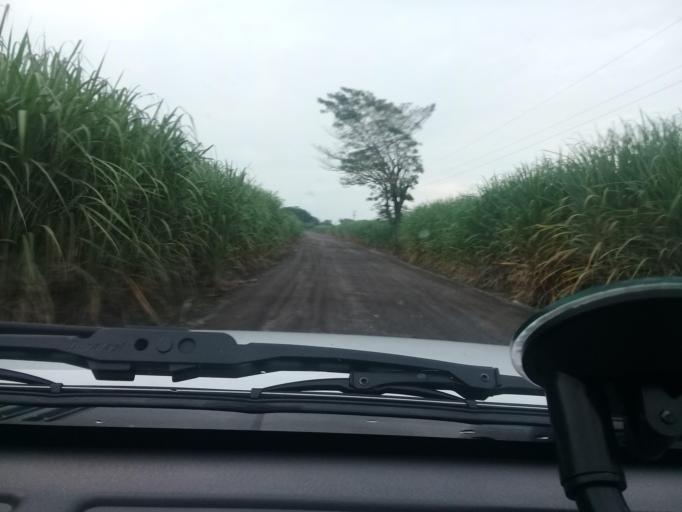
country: MX
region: Veracruz
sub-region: Puente Nacional
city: Cabezas
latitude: 19.3604
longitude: -96.4220
